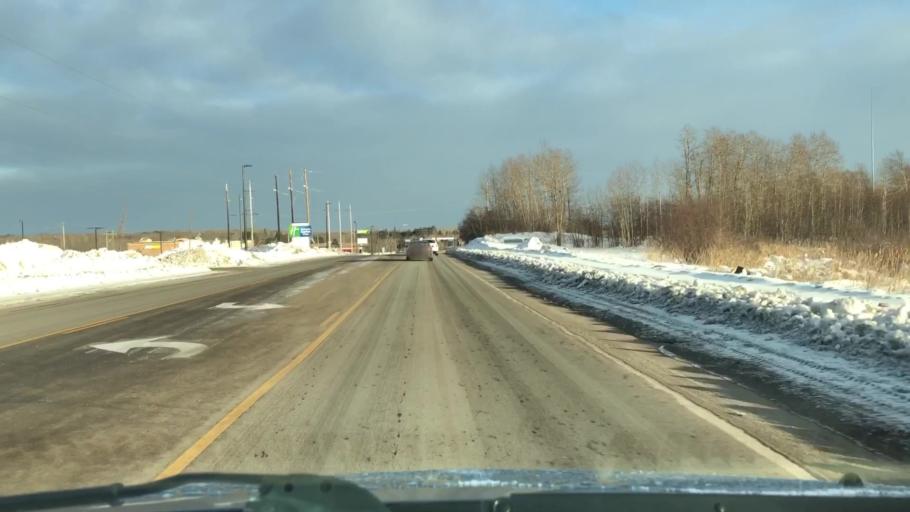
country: US
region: Minnesota
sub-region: Saint Louis County
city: Hermantown
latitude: 46.8130
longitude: -92.1791
